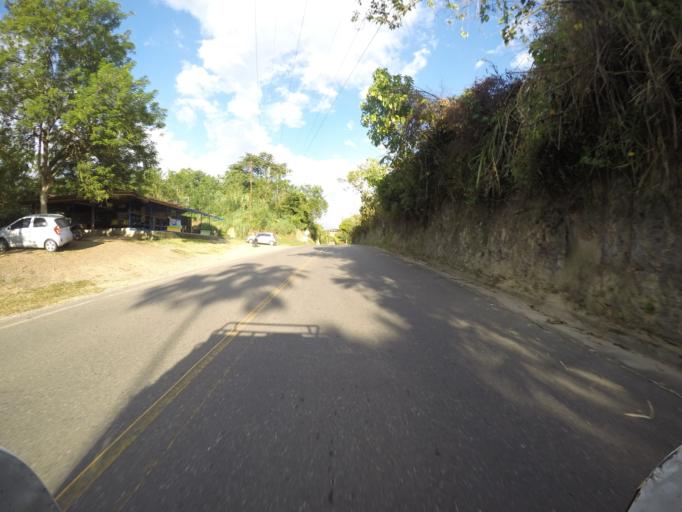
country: CO
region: Valle del Cauca
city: Alcala
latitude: 4.6871
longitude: -75.8141
